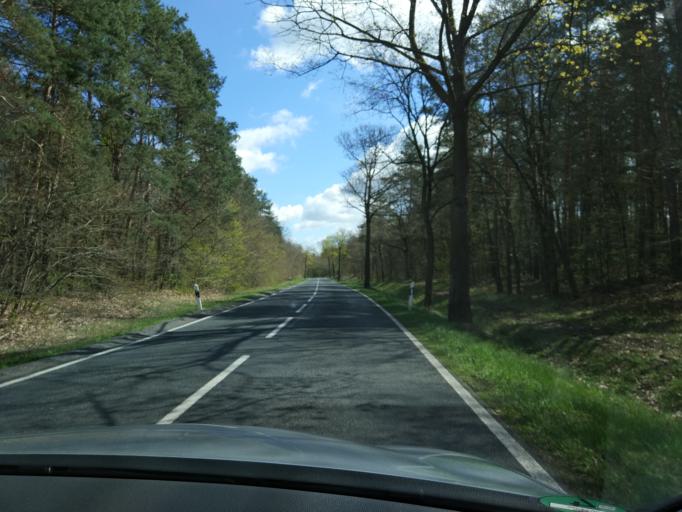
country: DE
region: Saxony-Anhalt
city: Radis
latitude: 51.7860
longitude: 12.4687
